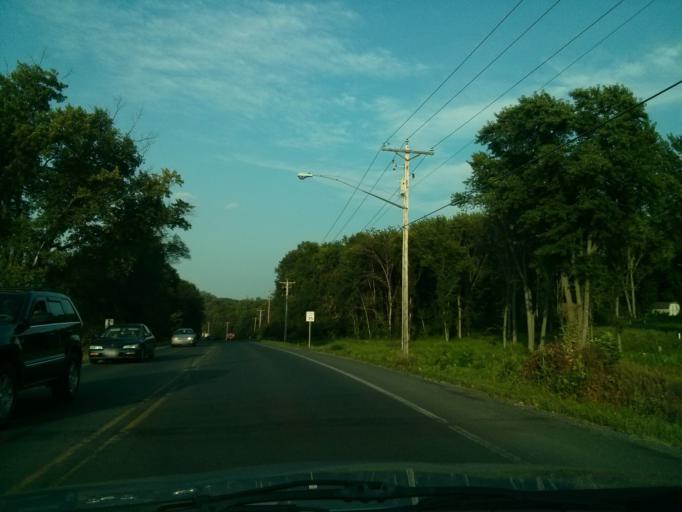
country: US
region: Wisconsin
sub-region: Saint Croix County
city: North Hudson
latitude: 45.0217
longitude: -92.6651
